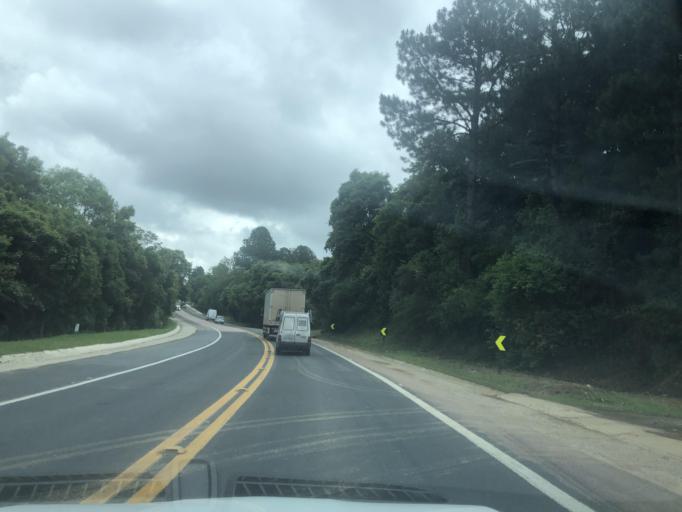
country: BR
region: Parana
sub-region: Lapa
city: Lapa
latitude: -25.8911
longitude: -49.5347
